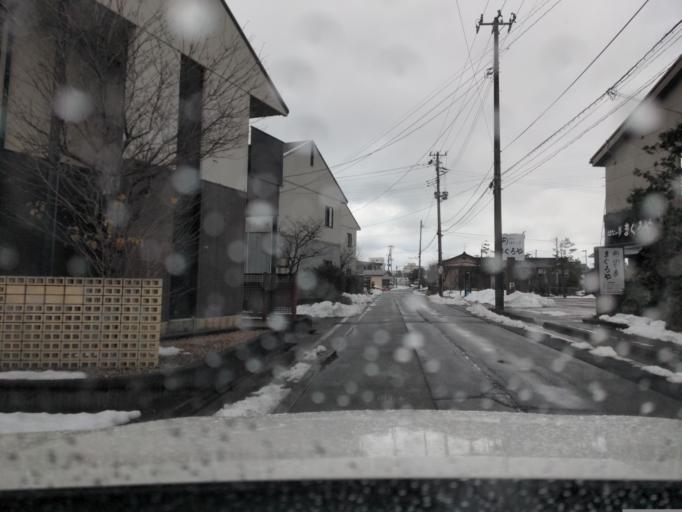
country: JP
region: Niigata
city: Kashiwazaki
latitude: 37.3661
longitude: 138.5726
